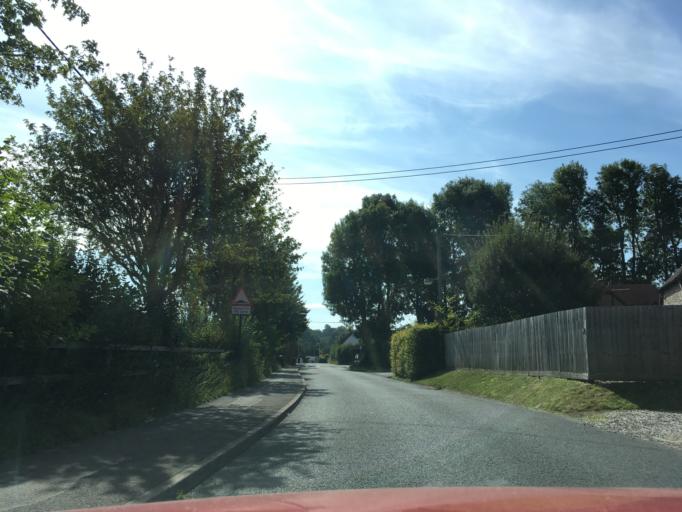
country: GB
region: England
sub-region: West Berkshire
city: Kintbury
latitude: 51.3983
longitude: -1.4505
